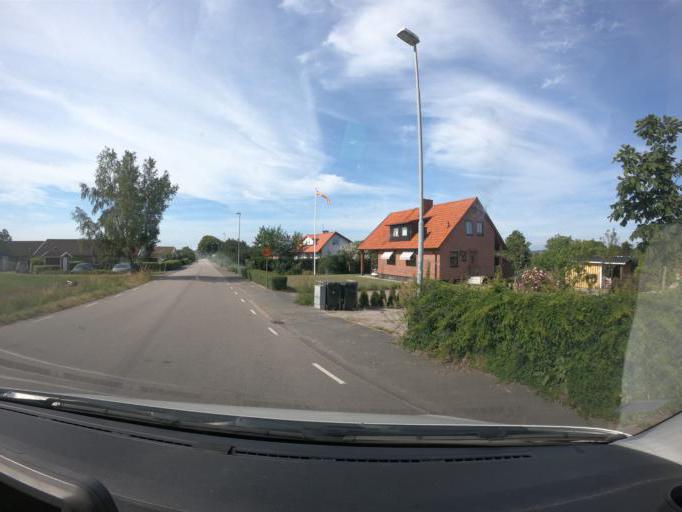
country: SE
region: Skane
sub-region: Angelholms Kommun
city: Vejbystrand
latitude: 56.3964
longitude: 12.6686
